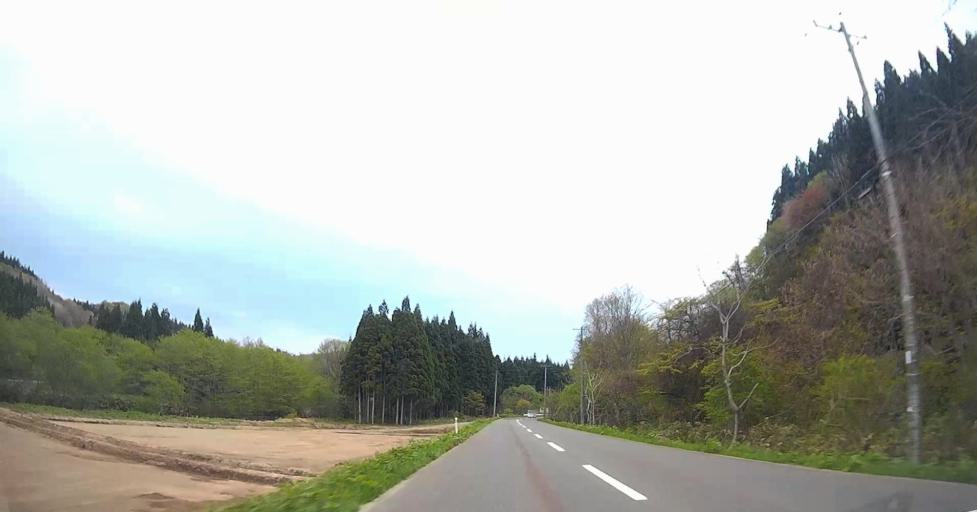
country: JP
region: Aomori
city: Goshogawara
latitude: 41.1218
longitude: 140.5225
